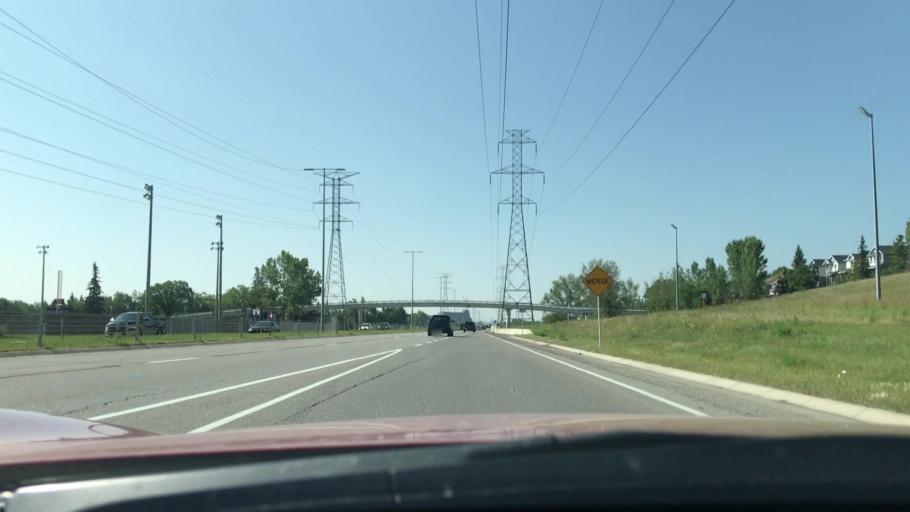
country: CA
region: Alberta
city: Calgary
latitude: 51.0335
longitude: -114.1645
